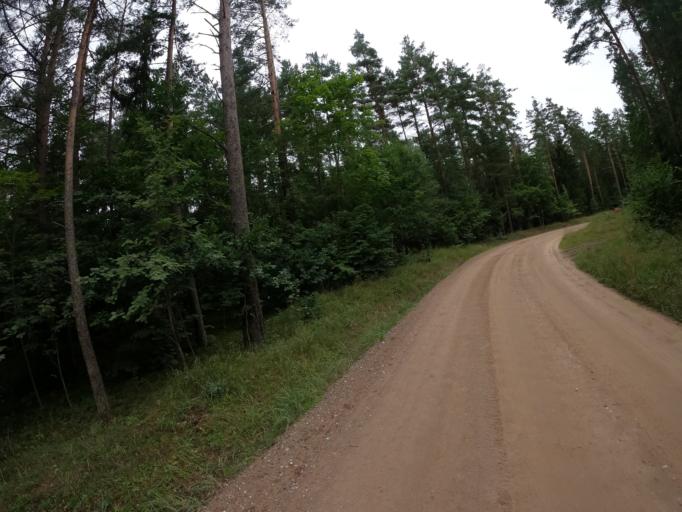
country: LV
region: Kuldigas Rajons
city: Kuldiga
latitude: 57.0113
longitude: 21.9829
